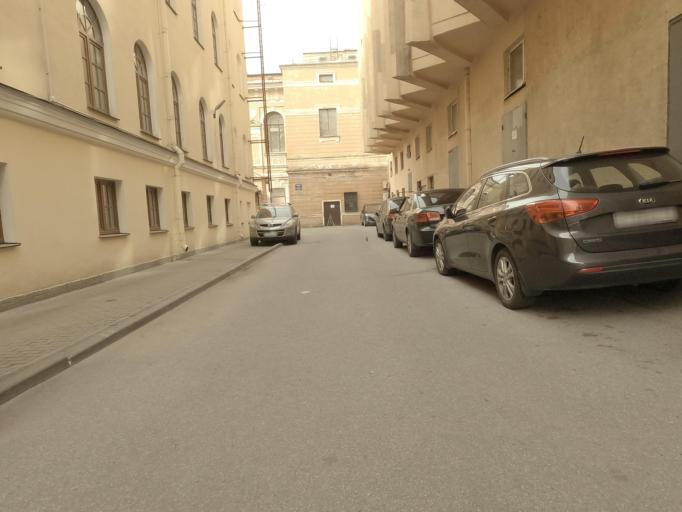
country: RU
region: St.-Petersburg
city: Admiralteisky
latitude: 59.9147
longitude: 30.2949
